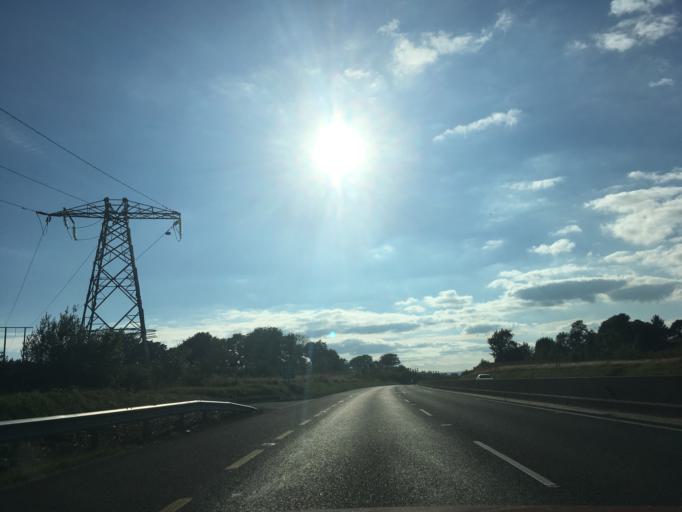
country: IE
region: Munster
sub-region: Waterford
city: Waterford
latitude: 52.2879
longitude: -7.0915
